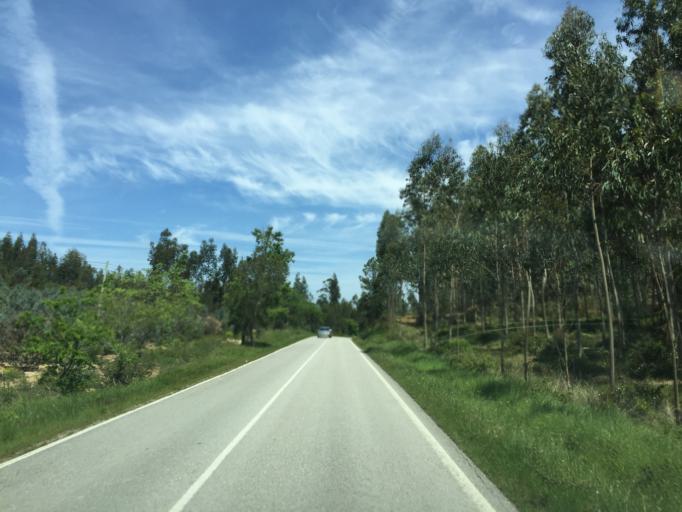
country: PT
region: Coimbra
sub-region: Soure
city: Soure
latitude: 40.0565
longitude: -8.6604
